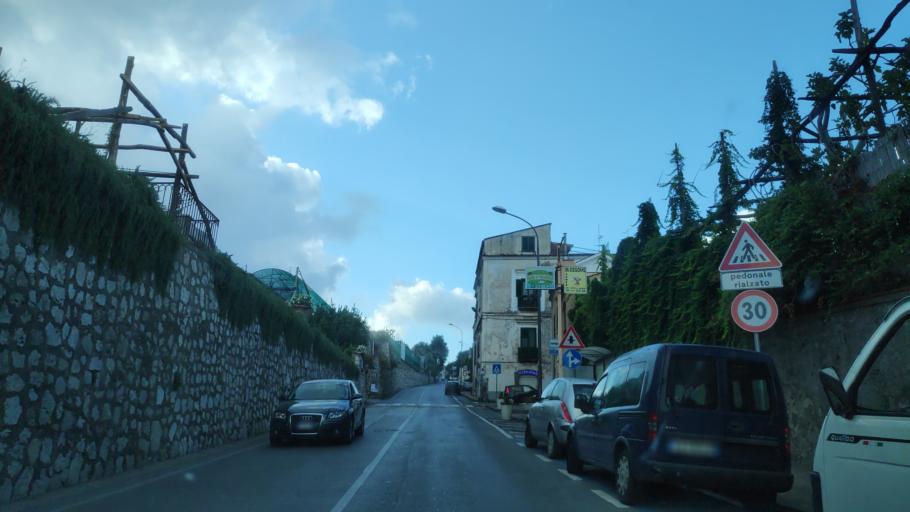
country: IT
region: Campania
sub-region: Provincia di Napoli
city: Piano di Sorrento
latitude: 40.6317
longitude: 14.4194
